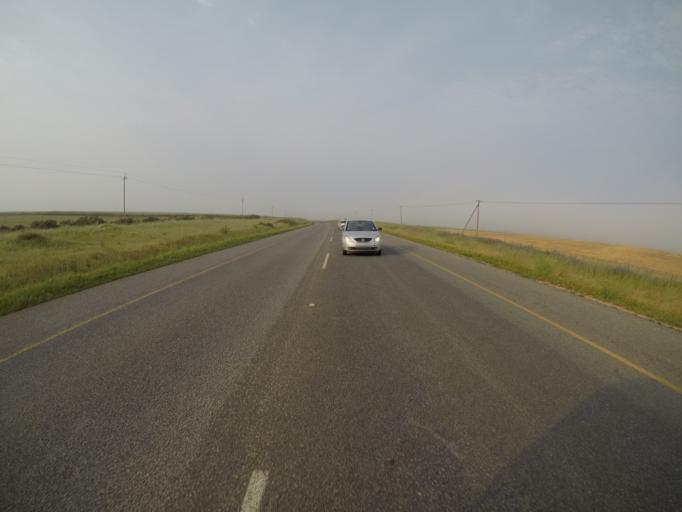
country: ZA
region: Western Cape
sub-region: West Coast District Municipality
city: Malmesbury
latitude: -33.6535
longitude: 18.7093
